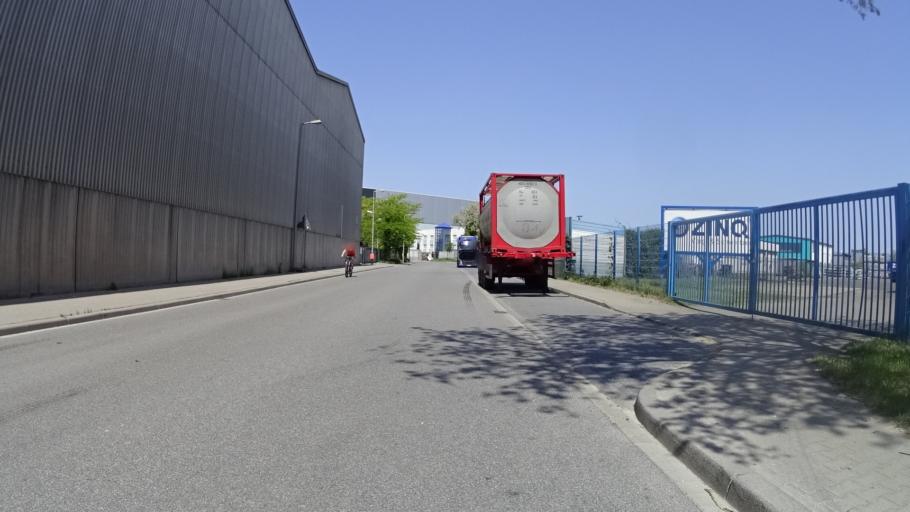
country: DE
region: Rheinland-Pfalz
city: Altrip
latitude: 49.4307
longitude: 8.5177
